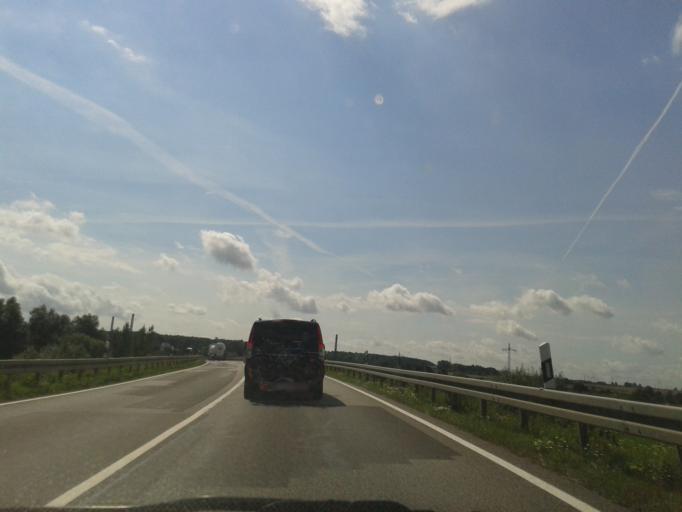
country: DE
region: Mecklenburg-Vorpommern
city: Pasewalk
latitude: 53.5076
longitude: 13.9763
